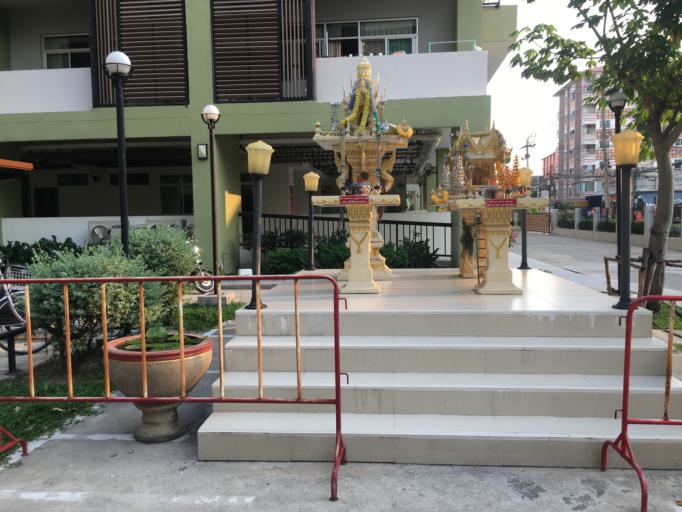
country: TH
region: Bangkok
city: Chatuchak
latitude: 13.8527
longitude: 100.5809
